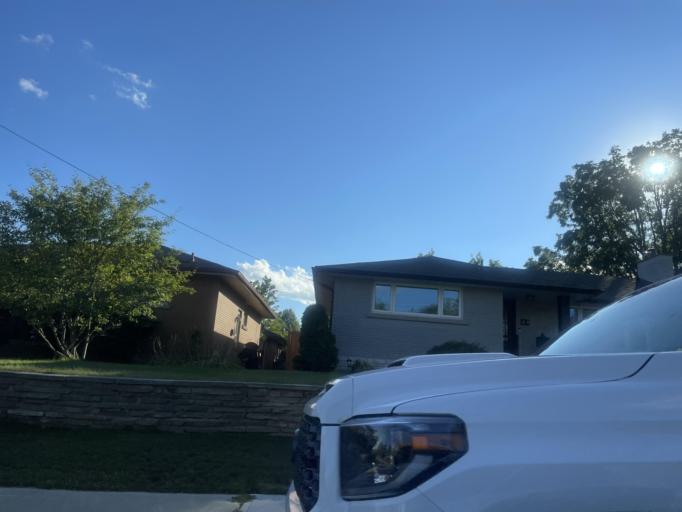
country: CA
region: Ontario
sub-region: Wellington County
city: Guelph
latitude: 43.5456
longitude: -80.2636
